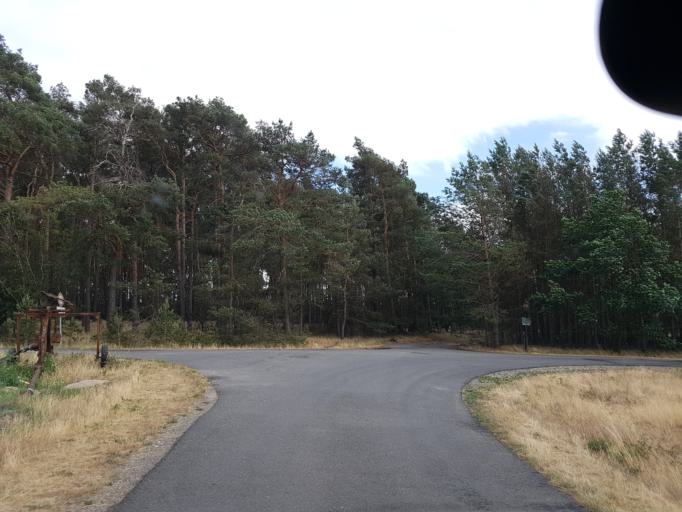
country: DE
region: Saxony-Anhalt
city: Jessen
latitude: 51.8279
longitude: 12.9650
